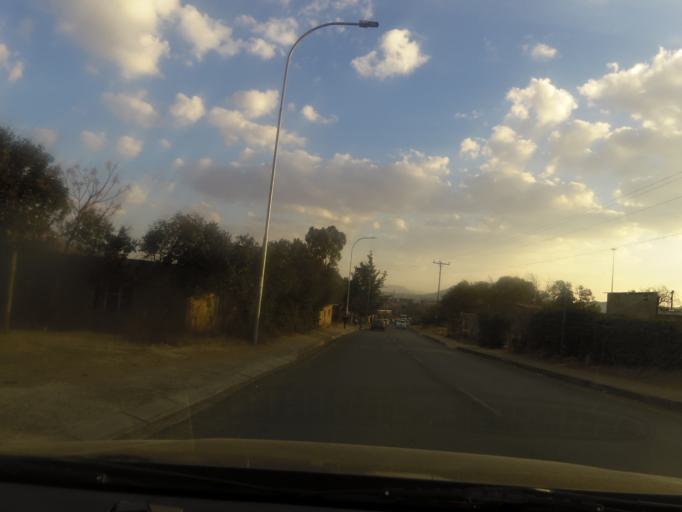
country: LS
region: Maseru
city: Maseru
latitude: -29.3044
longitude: 27.5335
